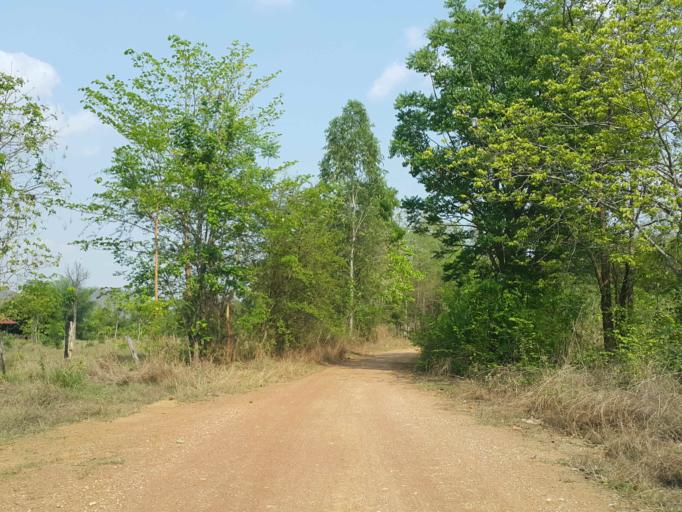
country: TH
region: Sukhothai
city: Thung Saliam
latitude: 17.3368
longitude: 99.4256
